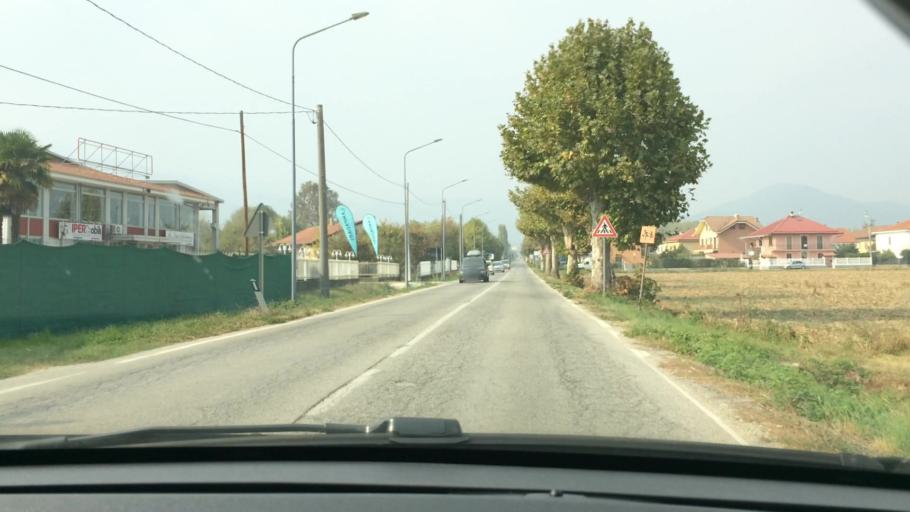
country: IT
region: Piedmont
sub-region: Provincia di Torino
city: Cumiana
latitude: 44.9586
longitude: 7.4051
